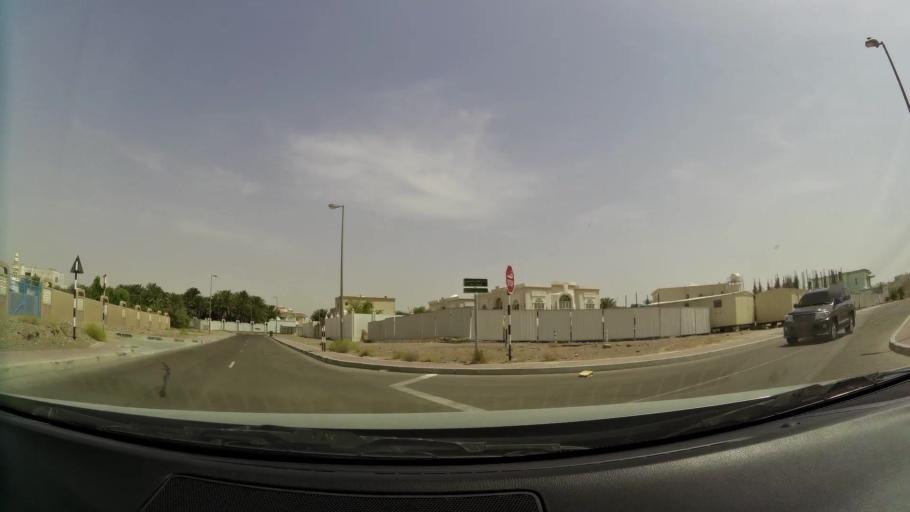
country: AE
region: Abu Dhabi
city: Al Ain
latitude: 24.1723
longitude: 55.7118
